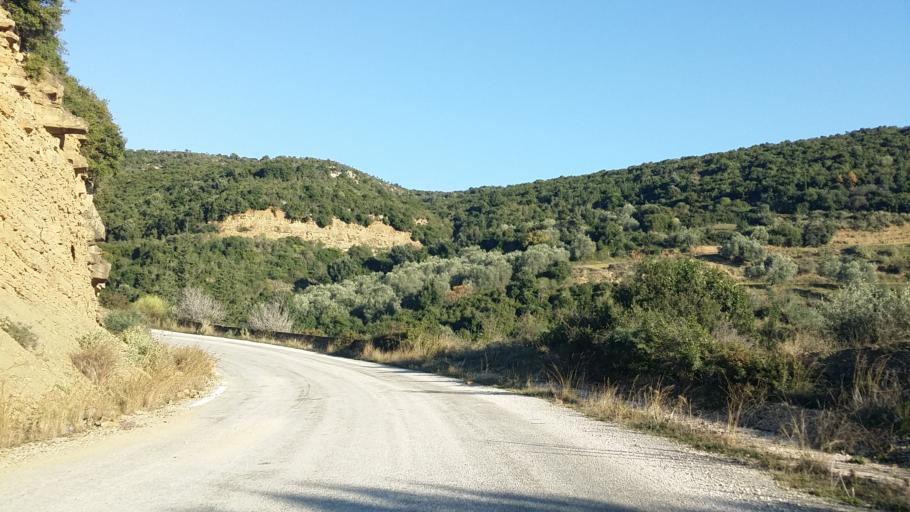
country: GR
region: West Greece
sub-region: Nomos Aitolias kai Akarnanias
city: Sardinia
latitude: 38.8901
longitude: 21.2314
